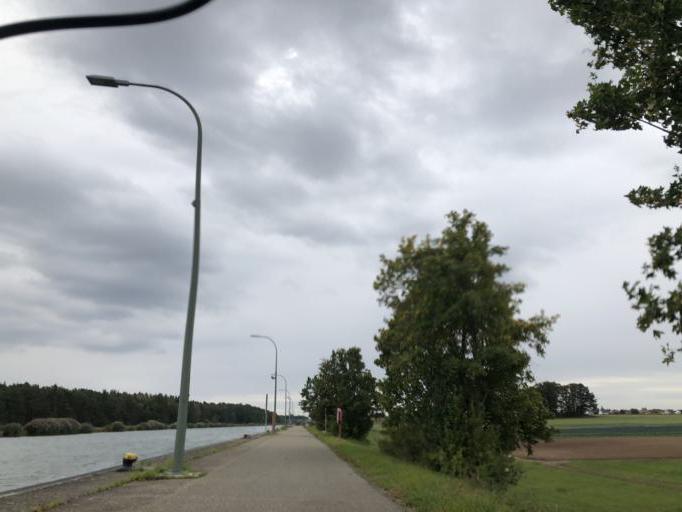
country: DE
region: Bavaria
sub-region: Regierungsbezirk Mittelfranken
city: Erlangen
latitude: 49.5531
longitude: 10.9692
